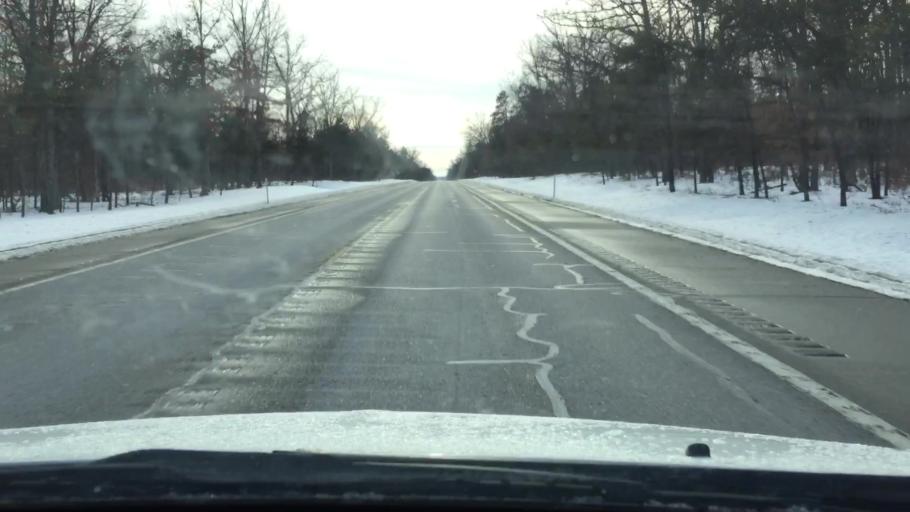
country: US
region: Michigan
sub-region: Wexford County
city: Manton
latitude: 44.5384
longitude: -85.3775
